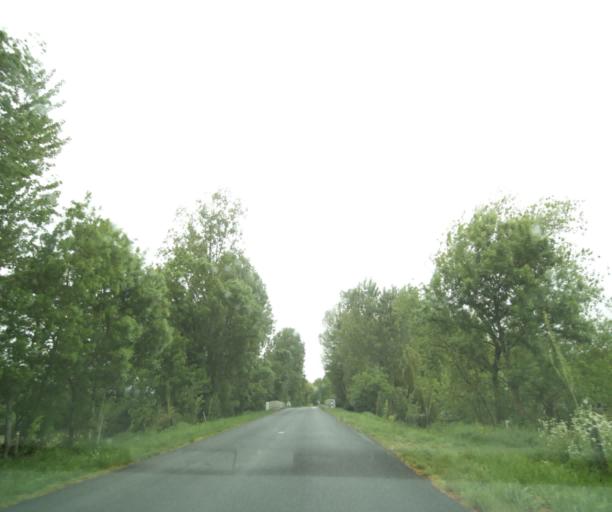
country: FR
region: Poitou-Charentes
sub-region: Departement de la Charente-Maritime
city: Pons
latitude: 45.6475
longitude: -0.5393
